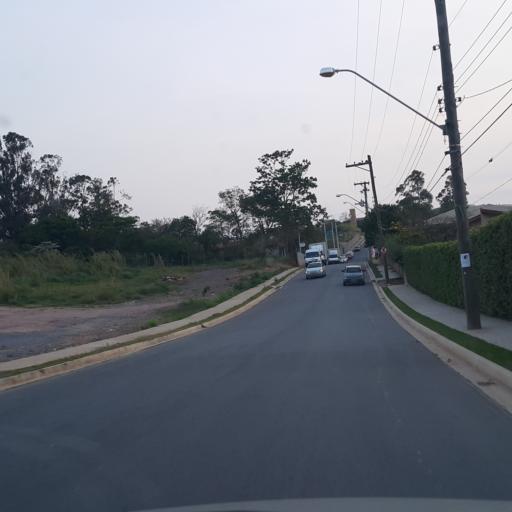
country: BR
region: Sao Paulo
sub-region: Vinhedo
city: Vinhedo
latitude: -23.0446
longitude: -46.9756
